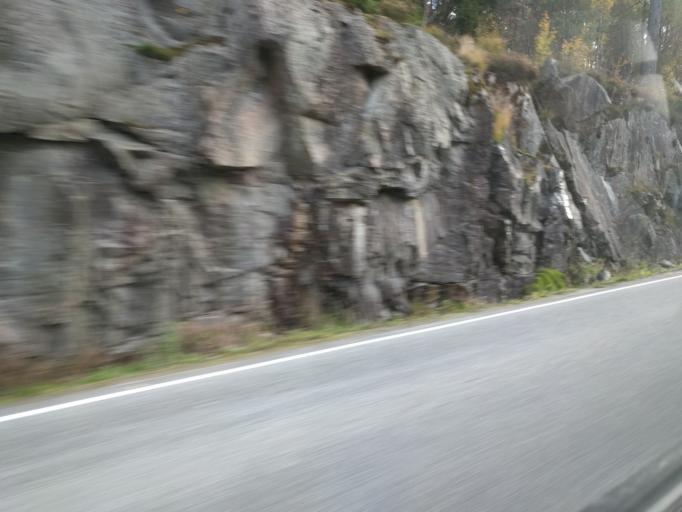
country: NO
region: Vest-Agder
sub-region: Songdalen
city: Nodeland
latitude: 58.2606
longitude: 7.8339
